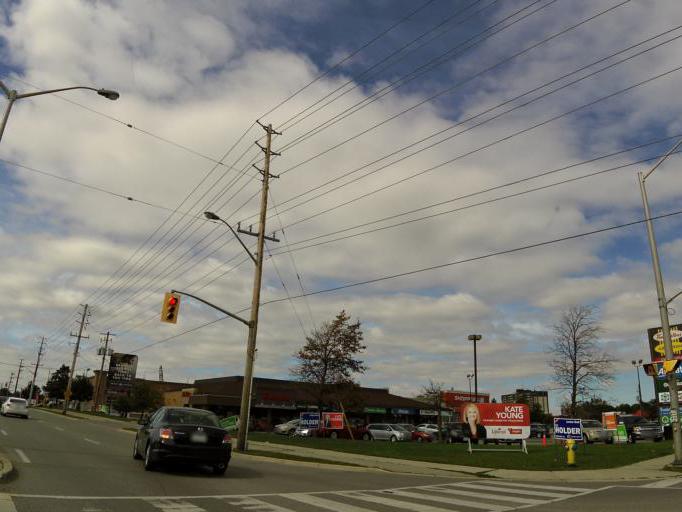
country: CA
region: Ontario
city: London
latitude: 42.9390
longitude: -81.2816
